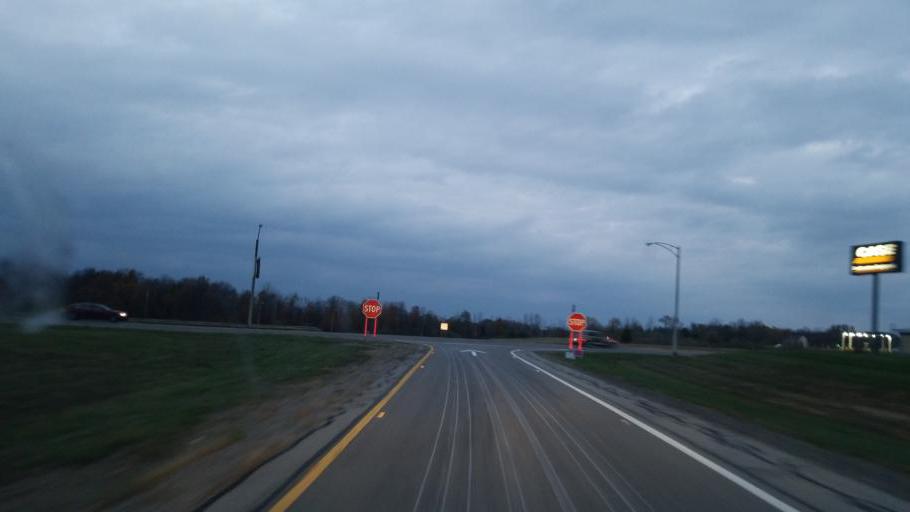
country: US
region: Ohio
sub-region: Richland County
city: Ontario
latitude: 40.7789
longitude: -82.6570
